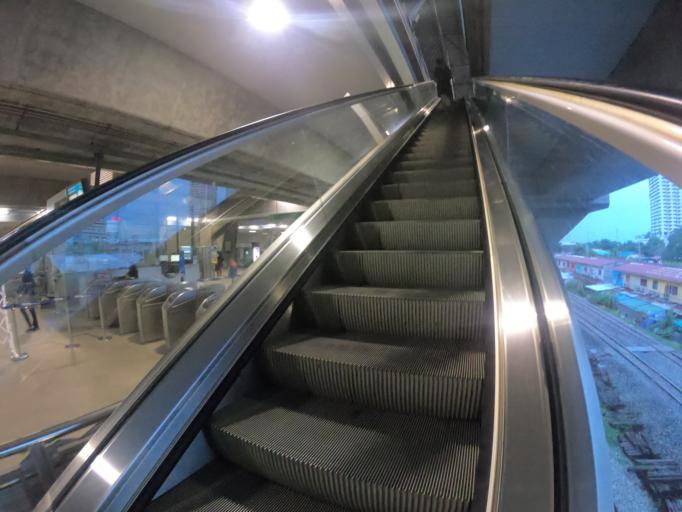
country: TH
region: Bangkok
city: Suan Luang
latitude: 13.7376
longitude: 100.6452
